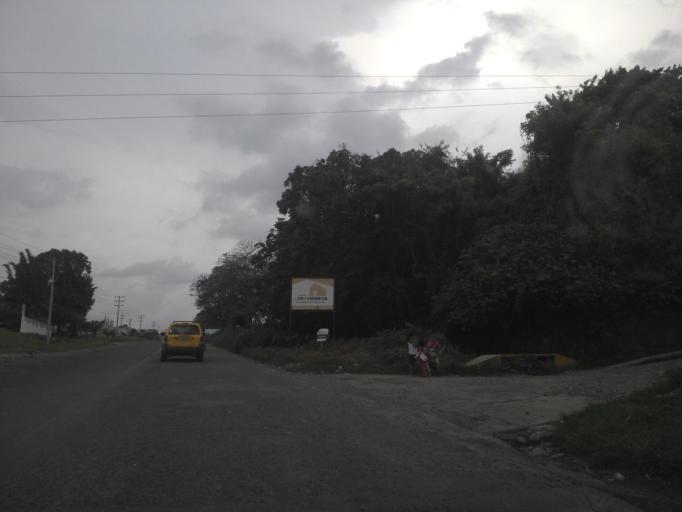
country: MX
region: Veracruz
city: Martinez de la Torre
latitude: 20.0802
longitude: -97.0387
